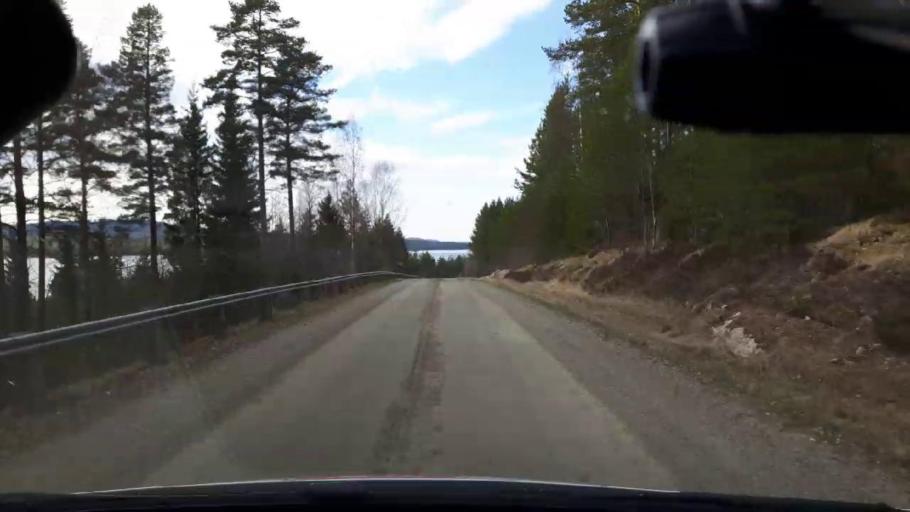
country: SE
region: Jaemtland
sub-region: Bergs Kommun
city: Hoverberg
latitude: 62.7220
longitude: 14.6728
